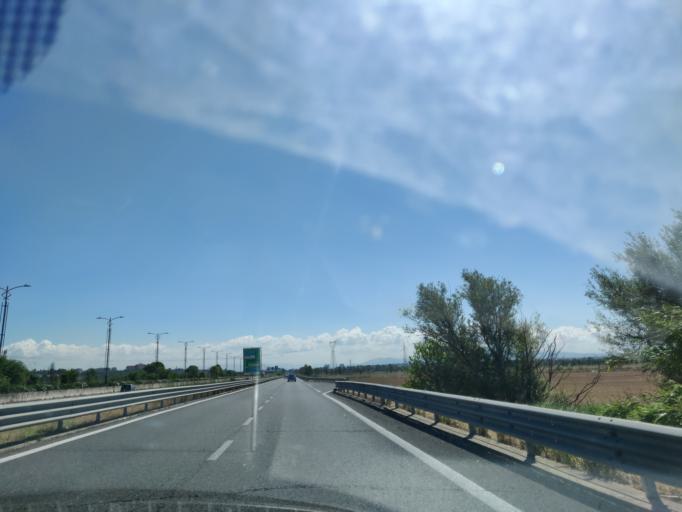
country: IT
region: Latium
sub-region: Citta metropolitana di Roma Capitale
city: Ponte Galeria-La Pisana
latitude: 41.8154
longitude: 12.3615
